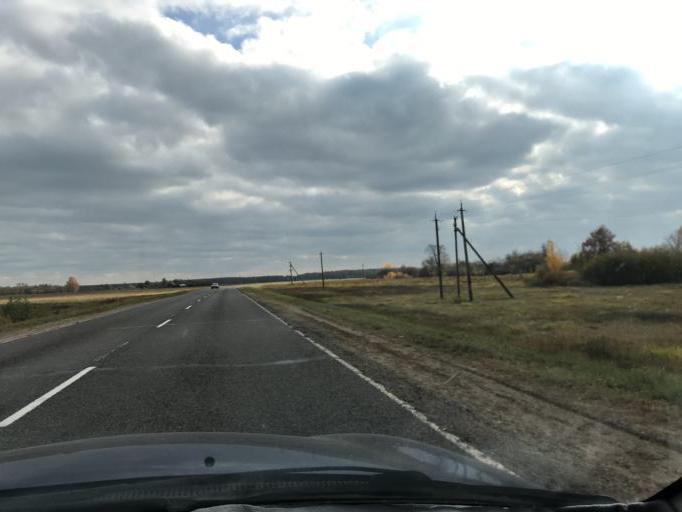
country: BY
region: Grodnenskaya
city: Lida
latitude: 53.7744
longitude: 25.1712
